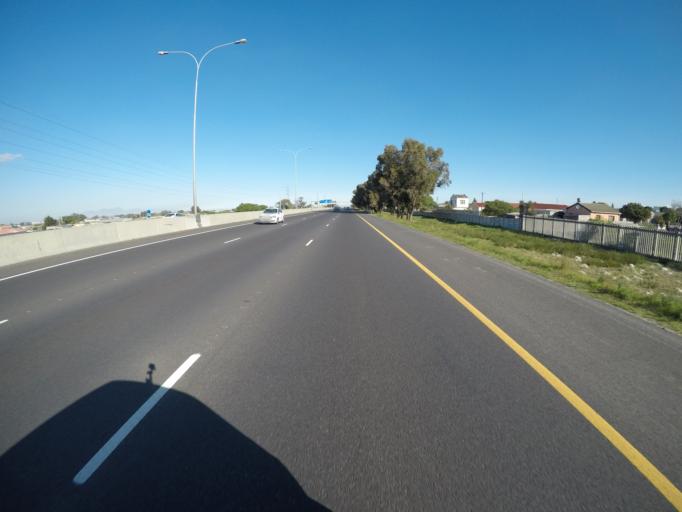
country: ZA
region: Western Cape
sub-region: City of Cape Town
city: Kraaifontein
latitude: -33.9408
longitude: 18.6600
